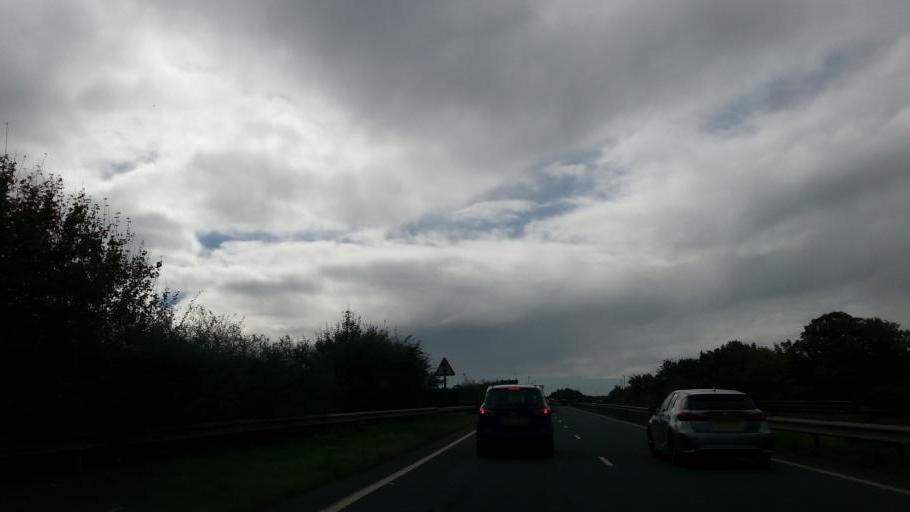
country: GB
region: England
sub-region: Gloucestershire
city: Gloucester
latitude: 51.8265
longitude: -2.2735
